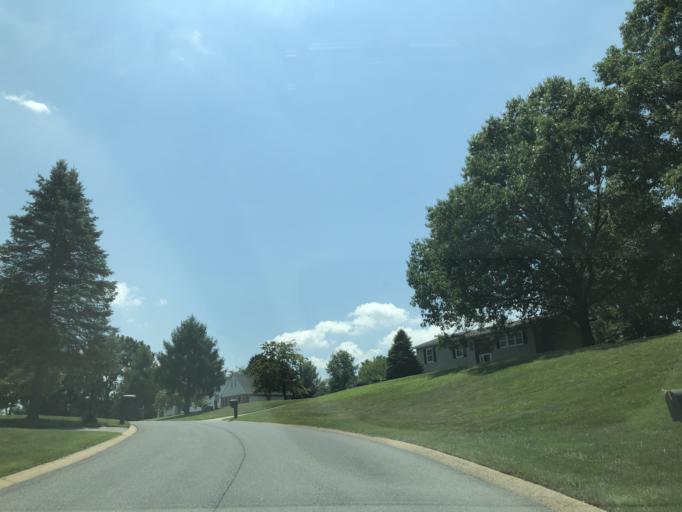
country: US
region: Maryland
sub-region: Carroll County
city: Westminster
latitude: 39.5288
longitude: -76.9564
